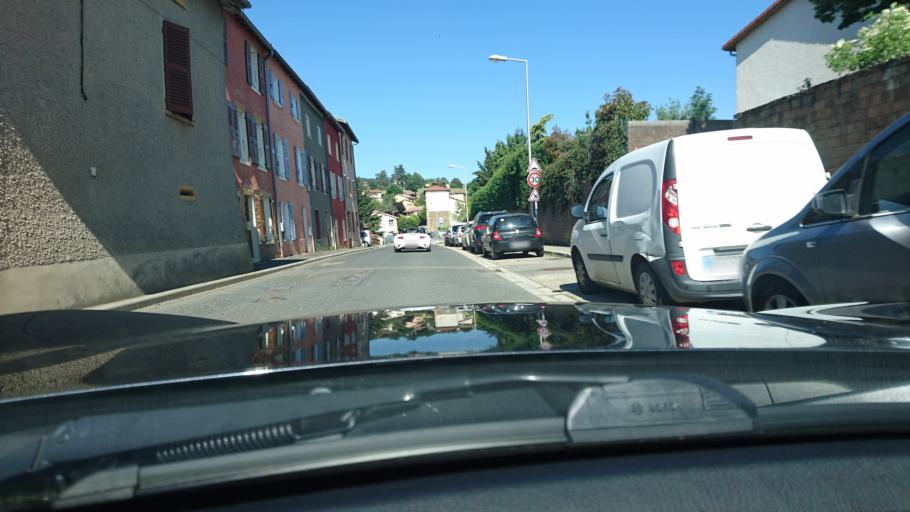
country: FR
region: Rhone-Alpes
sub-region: Departement du Rhone
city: Bessenay
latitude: 45.7760
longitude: 4.5509
